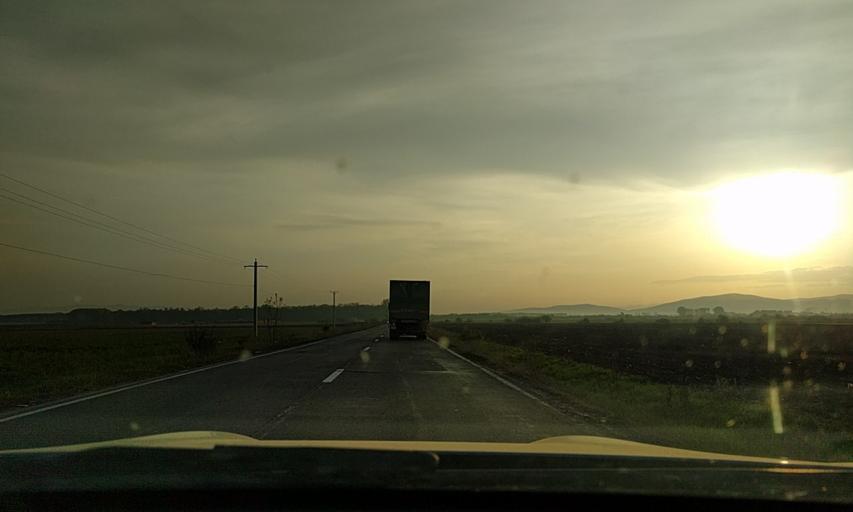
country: RO
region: Brasov
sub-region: Comuna Prejmer
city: Prejmer
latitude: 45.7227
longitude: 25.7255
